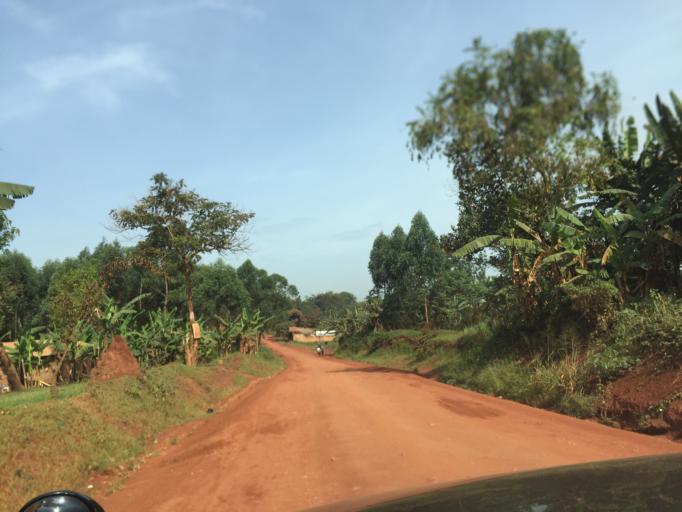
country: UG
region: Central Region
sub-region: Wakiso District
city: Wakiso
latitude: 0.4628
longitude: 32.5474
